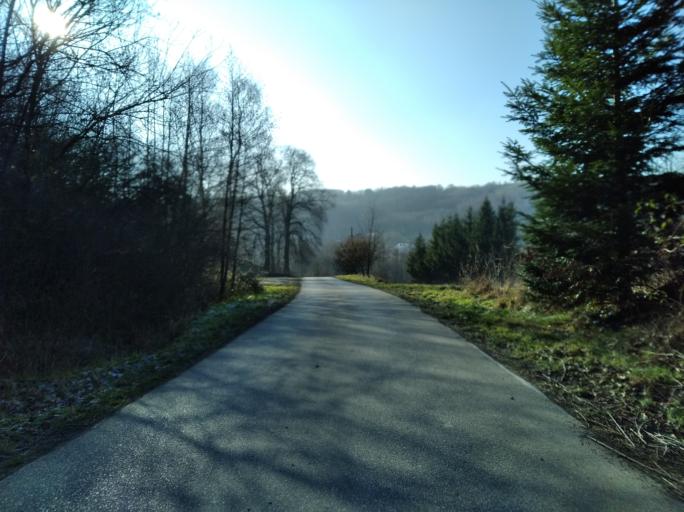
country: PL
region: Subcarpathian Voivodeship
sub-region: Powiat strzyzowski
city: Konieczkowa
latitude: 49.8518
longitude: 21.9196
